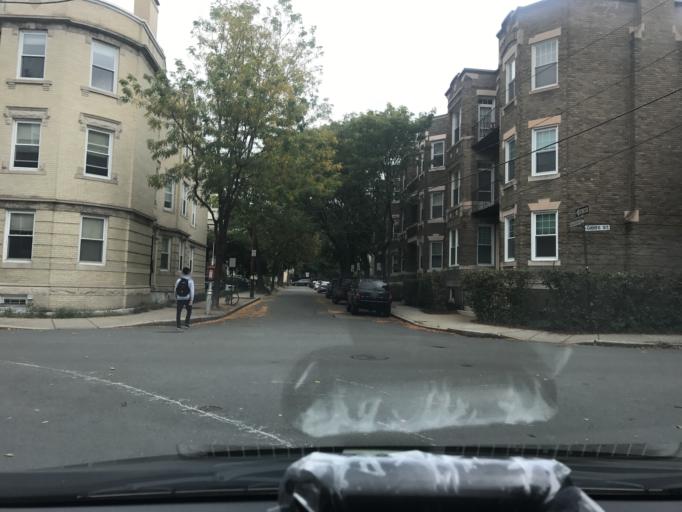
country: US
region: Massachusetts
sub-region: Norfolk County
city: Brookline
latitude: 42.3487
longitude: -71.1257
